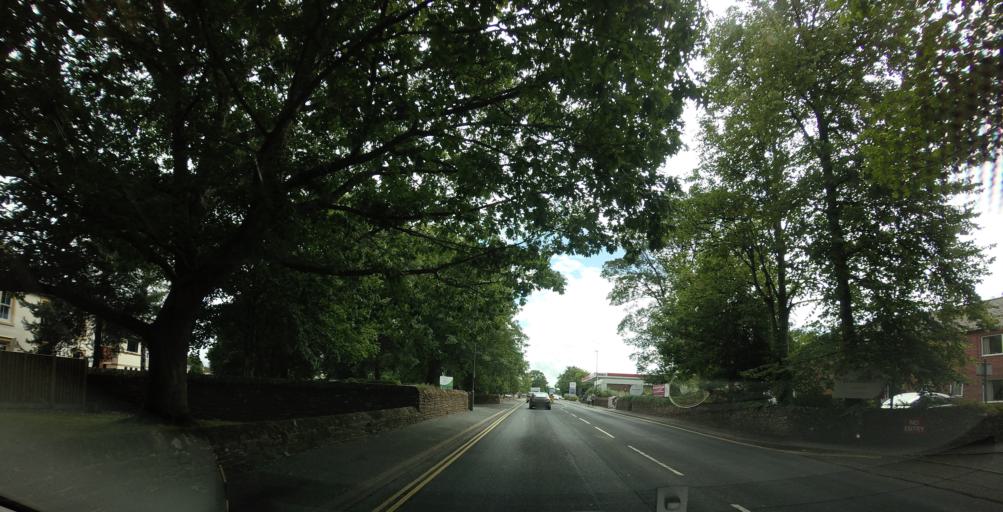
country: GB
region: England
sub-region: Cumbria
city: Penrith
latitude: 54.6583
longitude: -2.7460
